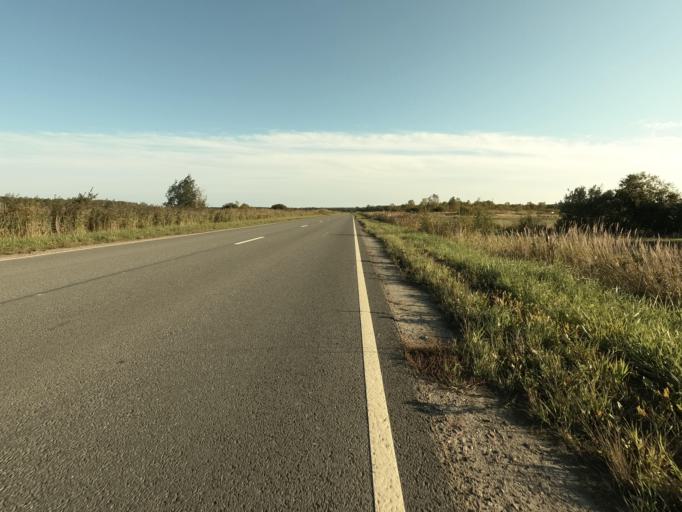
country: RU
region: St.-Petersburg
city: Sapernyy
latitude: 59.7354
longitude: 30.6556
